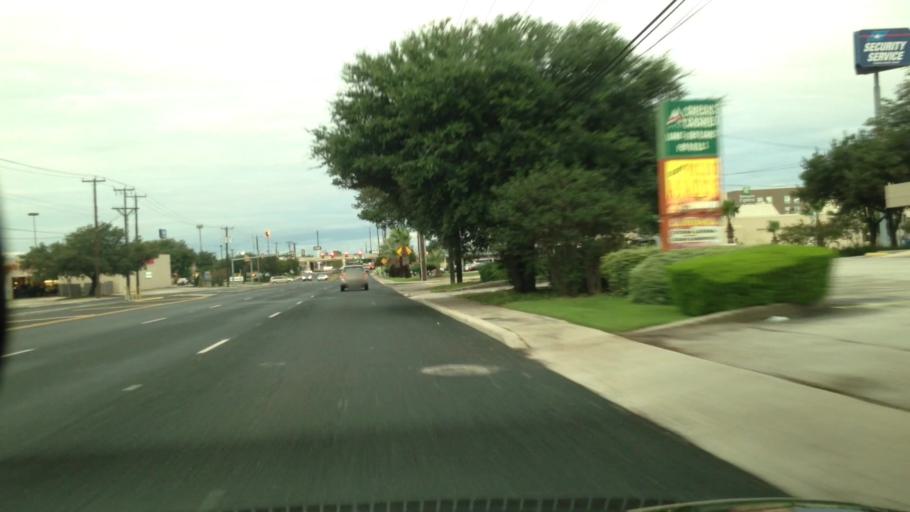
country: US
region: Texas
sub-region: Bexar County
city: Windcrest
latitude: 29.5104
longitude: -98.3929
